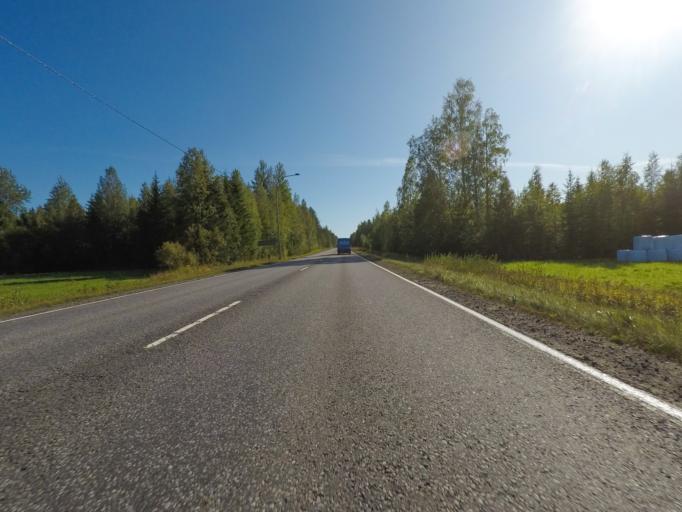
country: FI
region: Southern Savonia
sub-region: Pieksaemaeki
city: Joroinen
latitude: 62.1315
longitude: 27.8388
